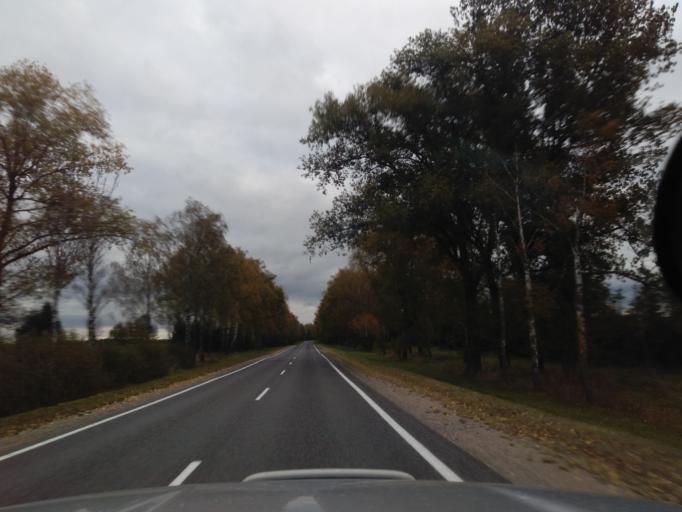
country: BY
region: Minsk
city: Slutsk
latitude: 53.2213
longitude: 27.4865
